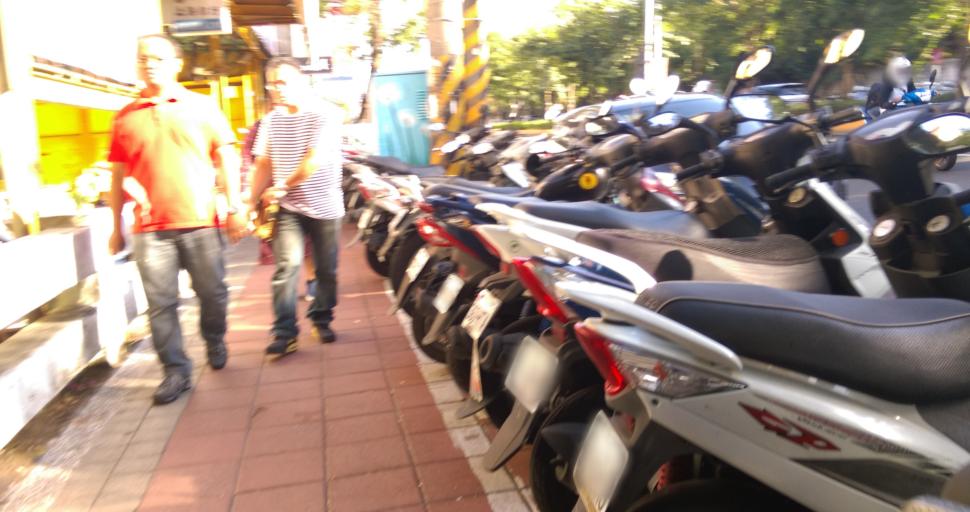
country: TW
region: Taiwan
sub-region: Hsinchu
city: Hsinchu
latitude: 24.7943
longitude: 121.0002
